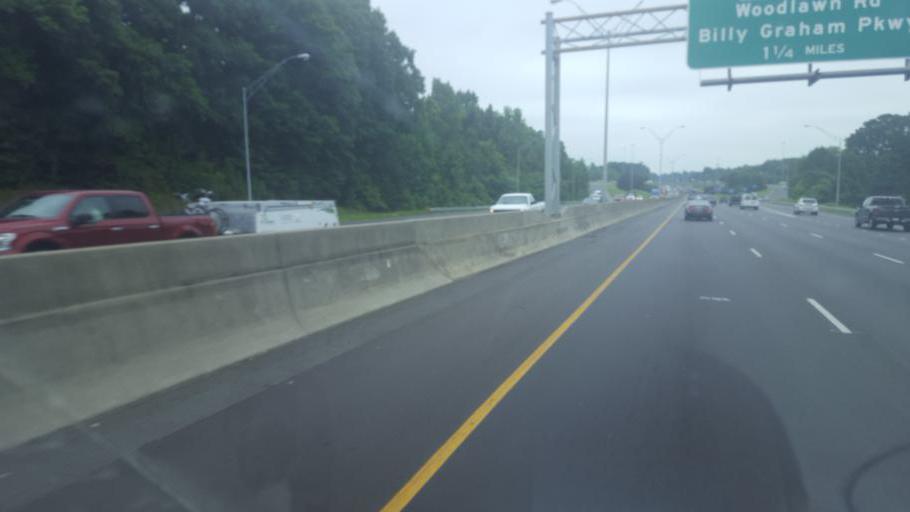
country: US
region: North Carolina
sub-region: Mecklenburg County
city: Pineville
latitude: 35.1579
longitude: -80.8916
